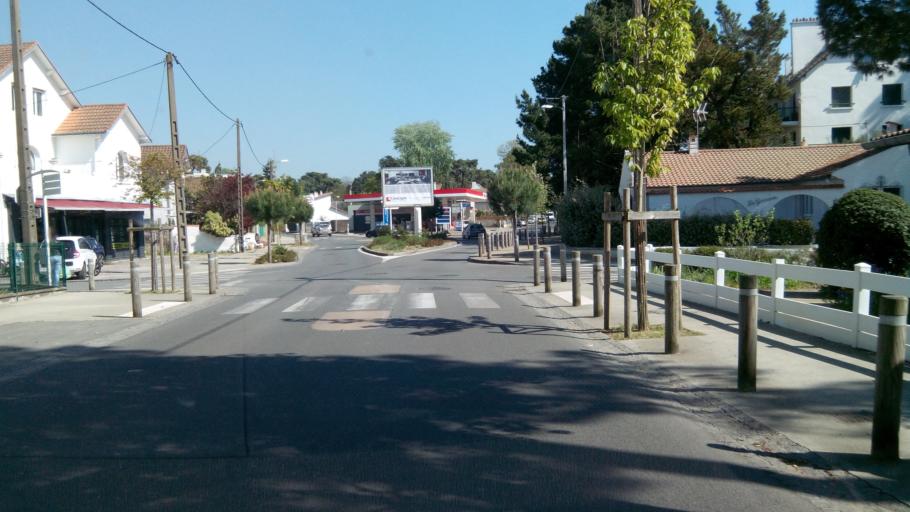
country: FR
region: Pays de la Loire
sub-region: Departement de la Loire-Atlantique
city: La Baule-Escoublac
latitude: 47.2876
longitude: -2.3818
